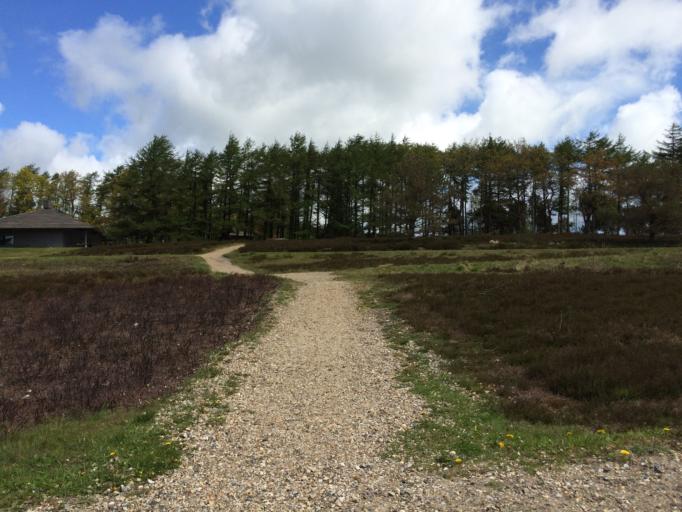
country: DK
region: Central Jutland
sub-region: Holstebro Kommune
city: Holstebro
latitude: 56.2296
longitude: 8.6201
